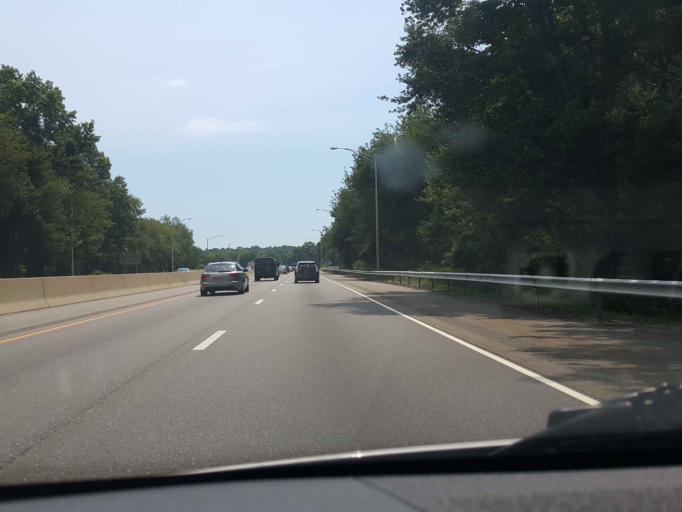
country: US
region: Connecticut
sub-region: New Haven County
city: Guilford
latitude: 41.2927
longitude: -72.6747
